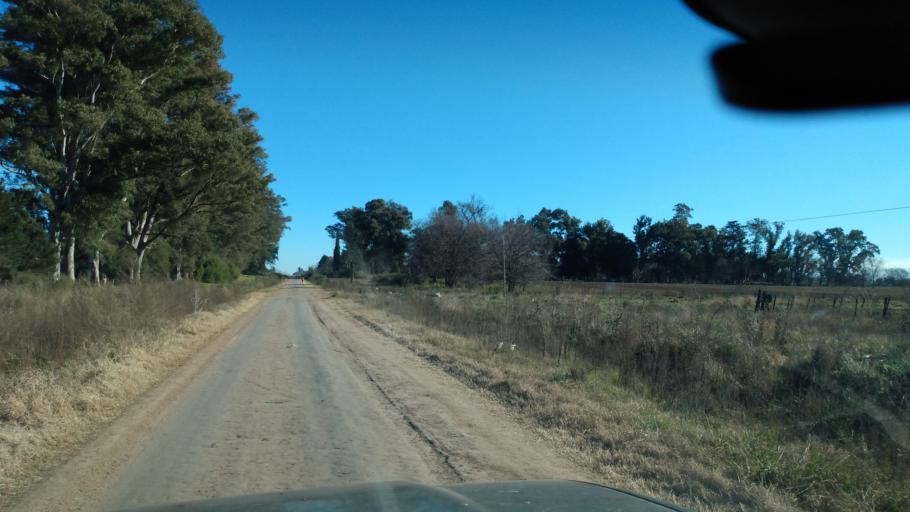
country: AR
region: Buenos Aires
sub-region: Partido de Lujan
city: Lujan
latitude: -34.5646
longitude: -59.1688
